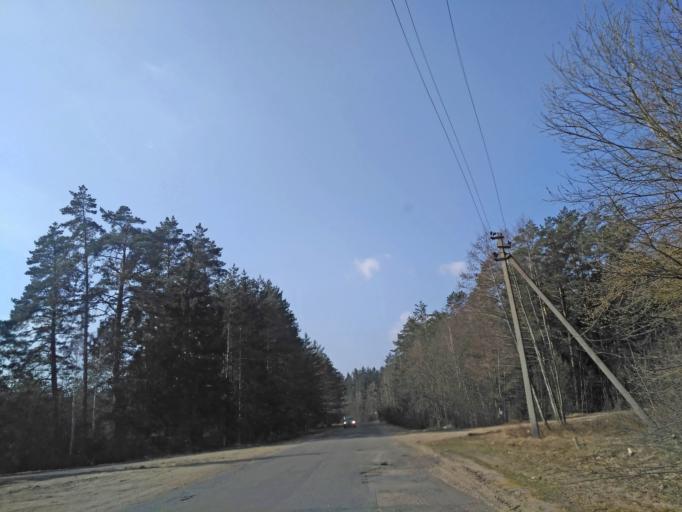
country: BY
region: Minsk
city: Horad Barysaw
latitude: 54.2449
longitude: 28.4530
